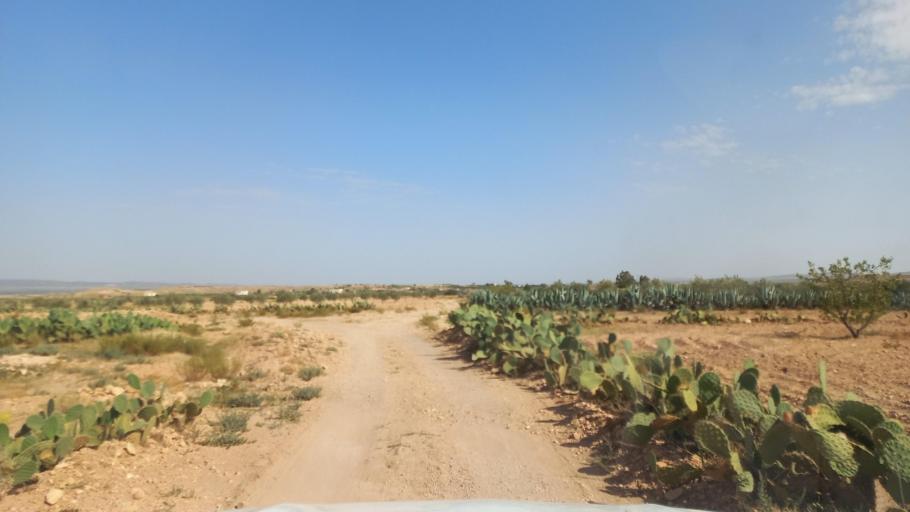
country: TN
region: Al Qasrayn
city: Kasserine
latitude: 35.2823
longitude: 8.9503
